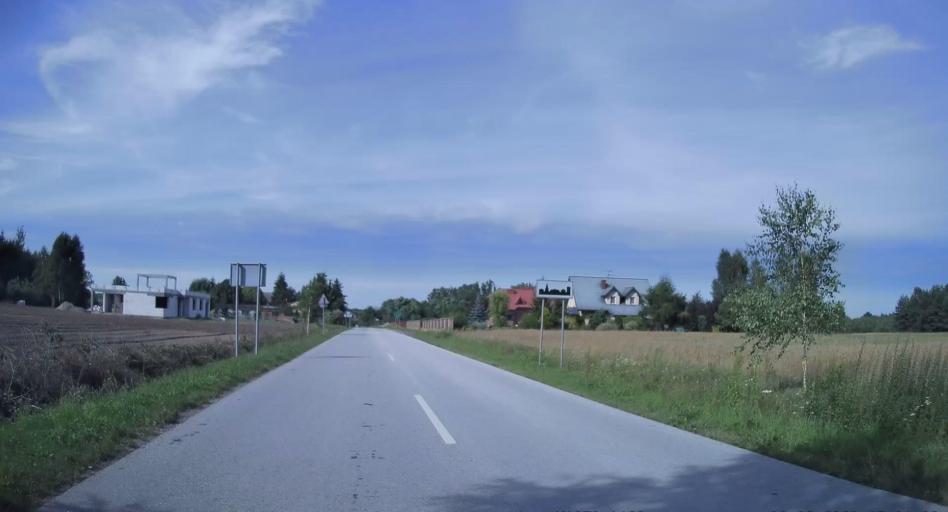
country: PL
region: Lodz Voivodeship
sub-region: Powiat opoczynski
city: Mniszkow
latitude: 51.3403
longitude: 20.0393
